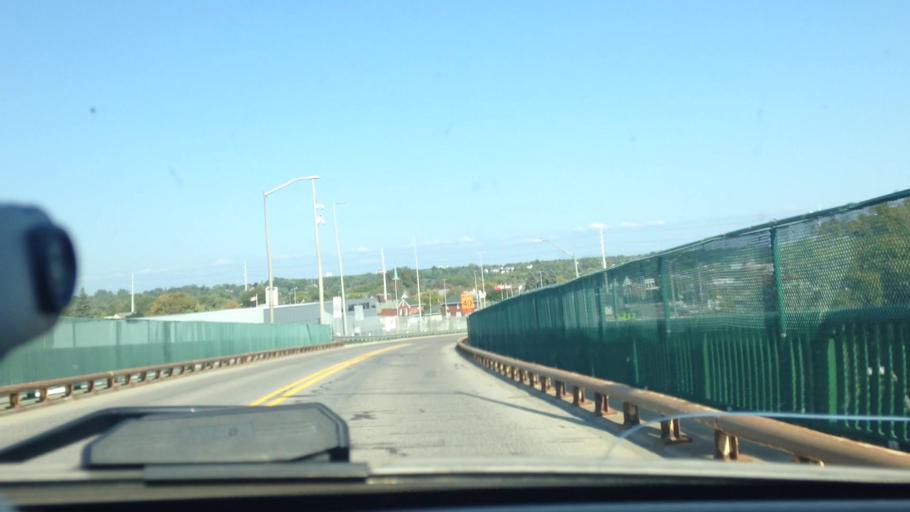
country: US
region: Michigan
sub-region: Chippewa County
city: Sault Ste. Marie
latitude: 46.5153
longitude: -84.3564
